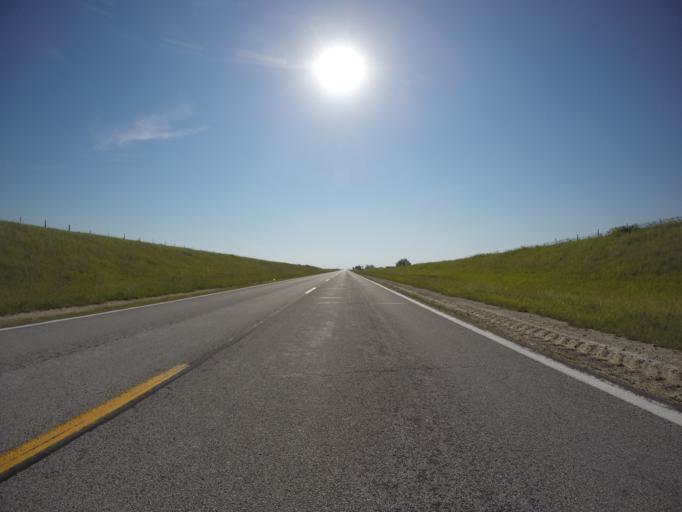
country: US
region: Nebraska
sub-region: Pawnee County
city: Pawnee City
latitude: 40.0447
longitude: -96.3633
